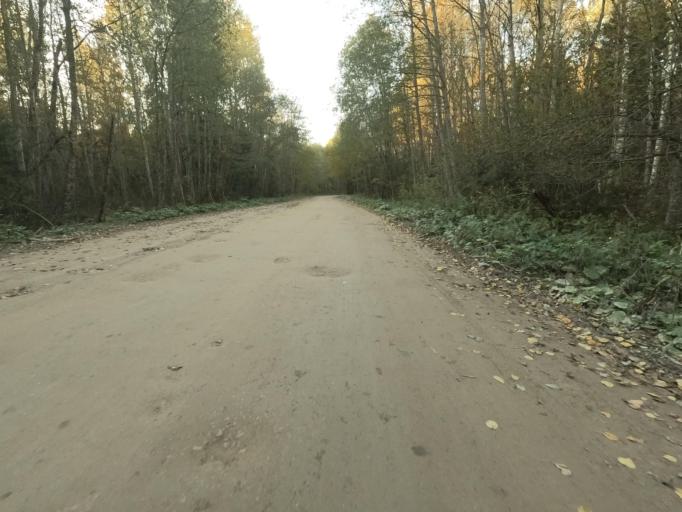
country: RU
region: Leningrad
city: Lyuban'
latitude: 59.0059
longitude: 31.0941
